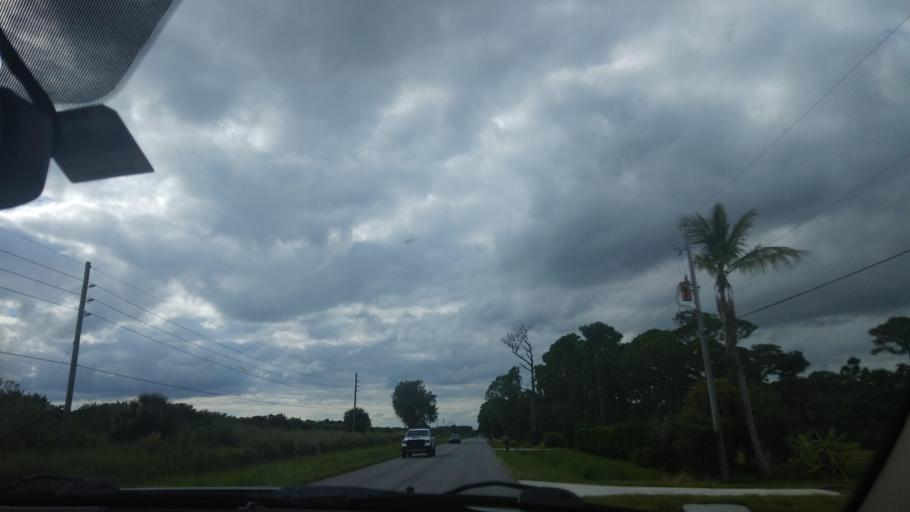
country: US
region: Florida
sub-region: Saint Lucie County
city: Lakewood Park
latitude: 27.5208
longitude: -80.3721
